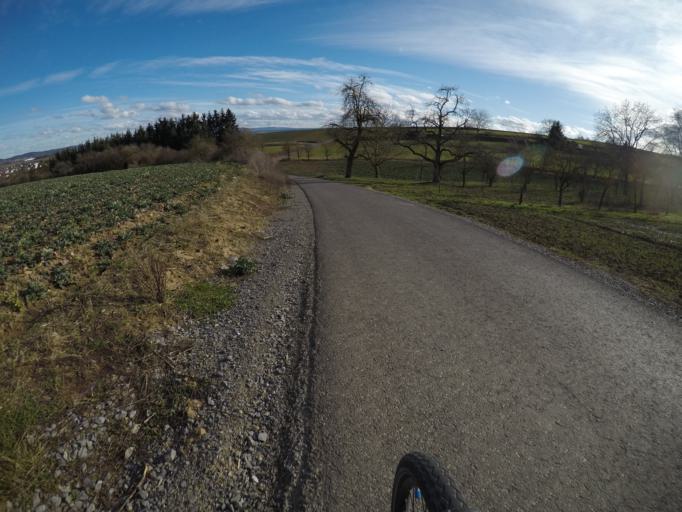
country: DE
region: Baden-Wuerttemberg
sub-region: Regierungsbezirk Stuttgart
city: Herrenberg
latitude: 48.5900
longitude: 8.8449
